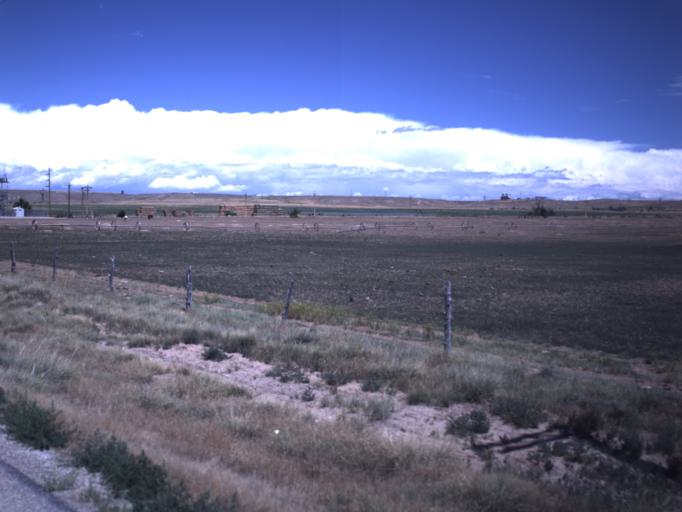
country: US
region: Utah
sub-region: Uintah County
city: Naples
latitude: 40.2009
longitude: -109.6648
